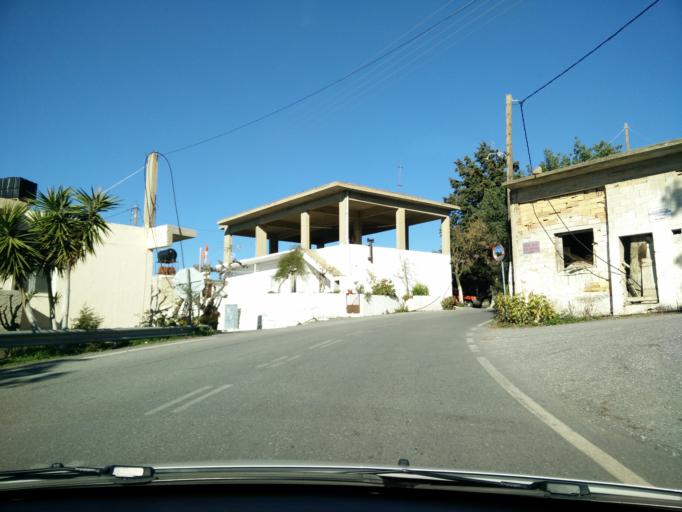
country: GR
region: Crete
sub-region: Nomos Irakleiou
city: Arkalochori
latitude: 35.0775
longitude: 25.3592
